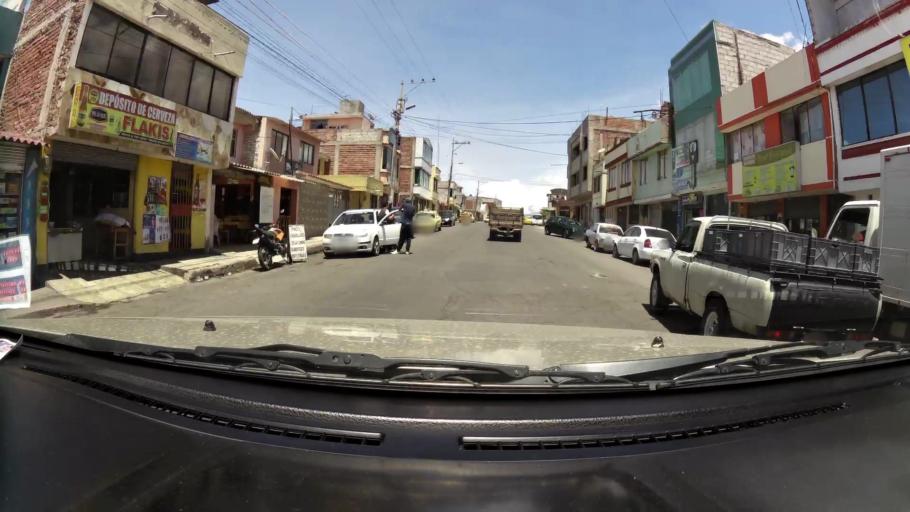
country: EC
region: Chimborazo
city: Riobamba
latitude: -1.6827
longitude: -78.6343
